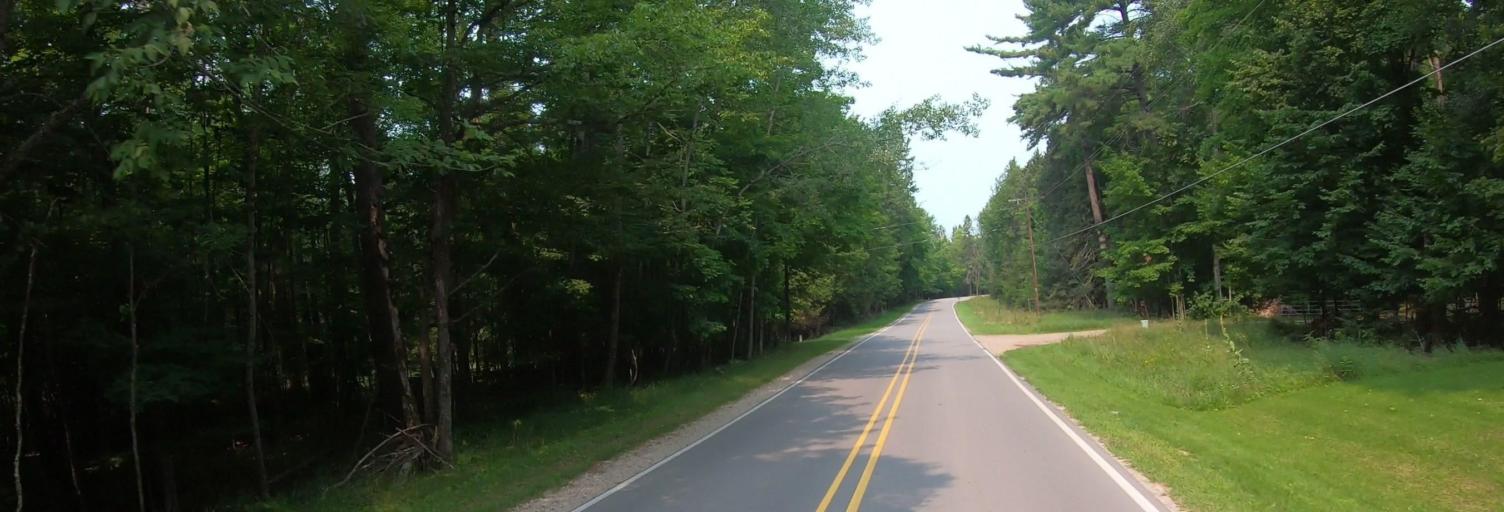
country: CA
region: Ontario
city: Thessalon
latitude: 46.0243
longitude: -83.7329
